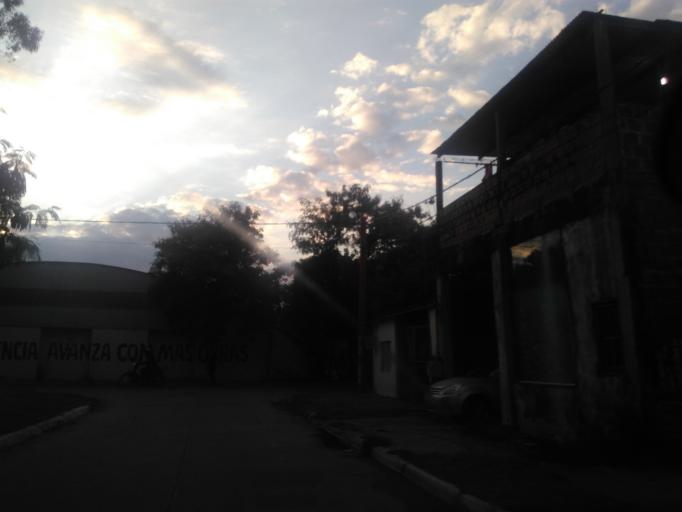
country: AR
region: Chaco
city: Resistencia
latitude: -27.4545
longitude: -59.0181
